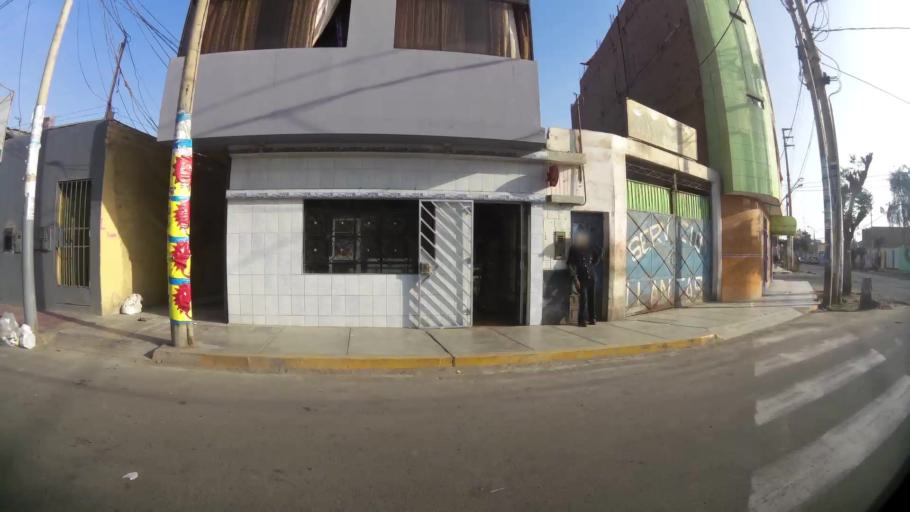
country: PE
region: Lima
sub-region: Huaura
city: Huacho
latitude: -11.1112
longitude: -77.6065
